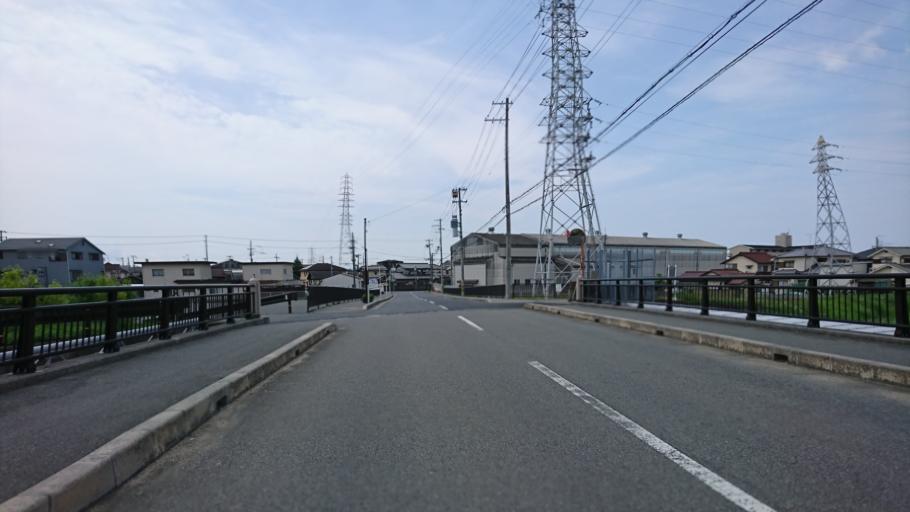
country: JP
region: Hyogo
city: Kakogawacho-honmachi
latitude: 34.7288
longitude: 134.9117
